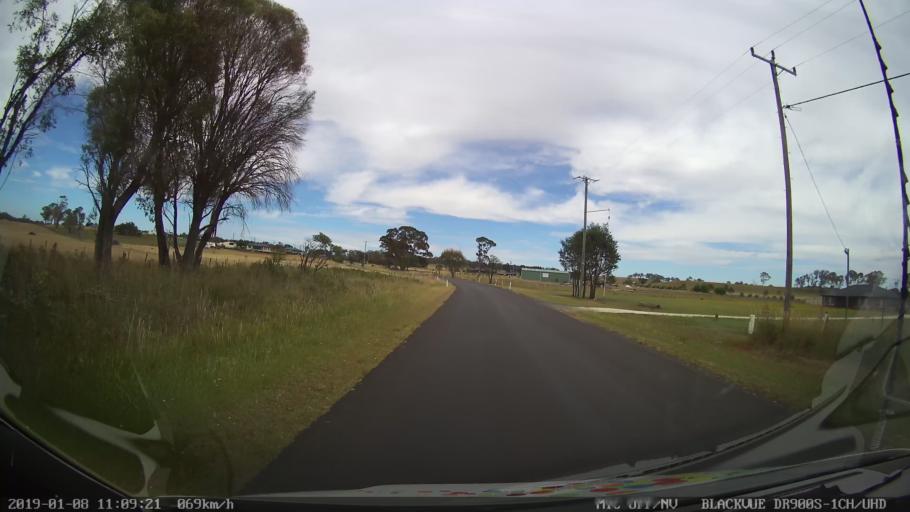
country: AU
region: New South Wales
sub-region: Guyra
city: Guyra
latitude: -30.2252
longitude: 151.6481
